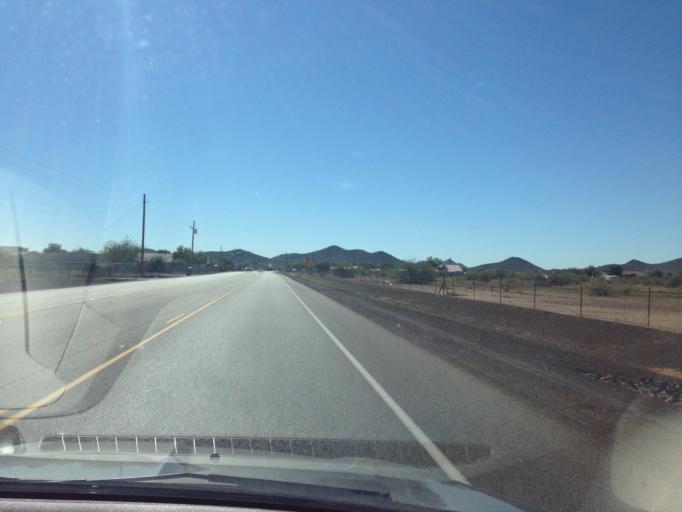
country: US
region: Arizona
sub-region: Maricopa County
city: Anthem
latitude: 33.8161
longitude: -112.0654
